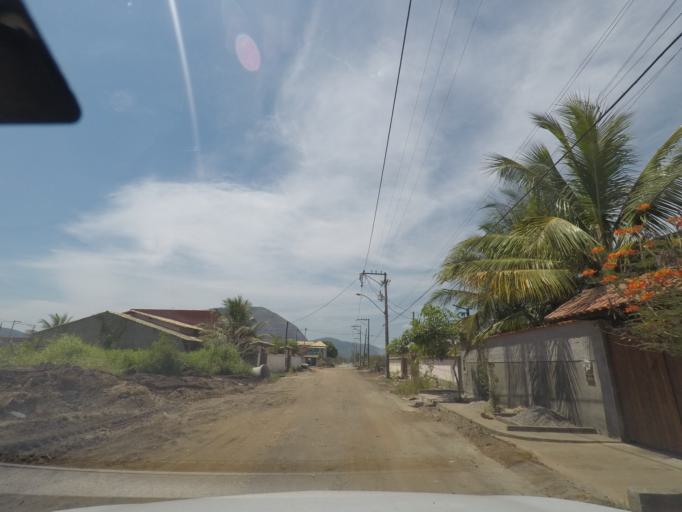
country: BR
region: Rio de Janeiro
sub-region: Marica
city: Marica
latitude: -22.9603
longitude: -42.9550
